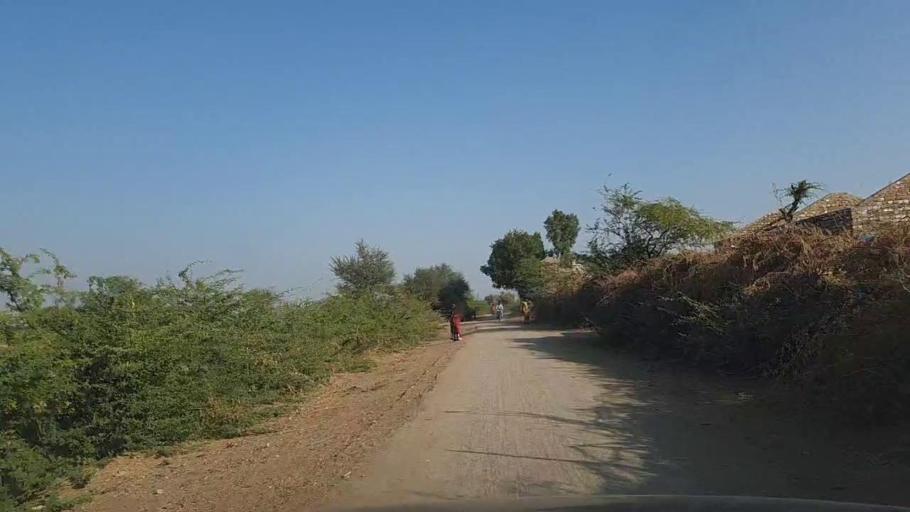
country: PK
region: Sindh
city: Digri
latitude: 25.0401
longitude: 69.2681
